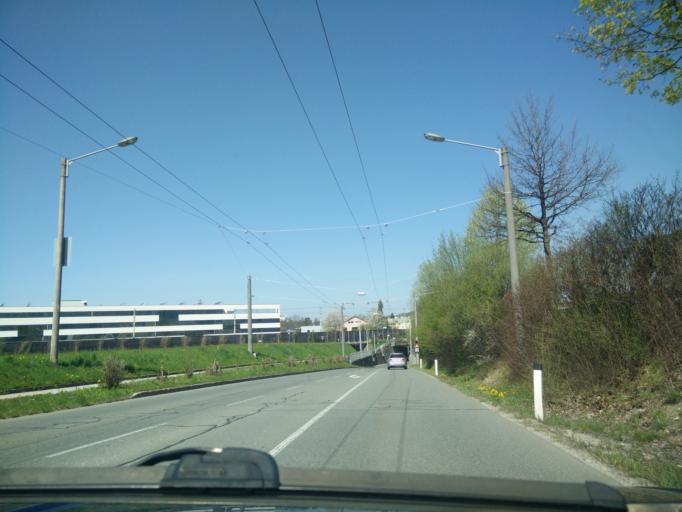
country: AT
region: Salzburg
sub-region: Politischer Bezirk Salzburg-Umgebung
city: Elsbethen
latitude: 47.7765
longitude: 13.0825
